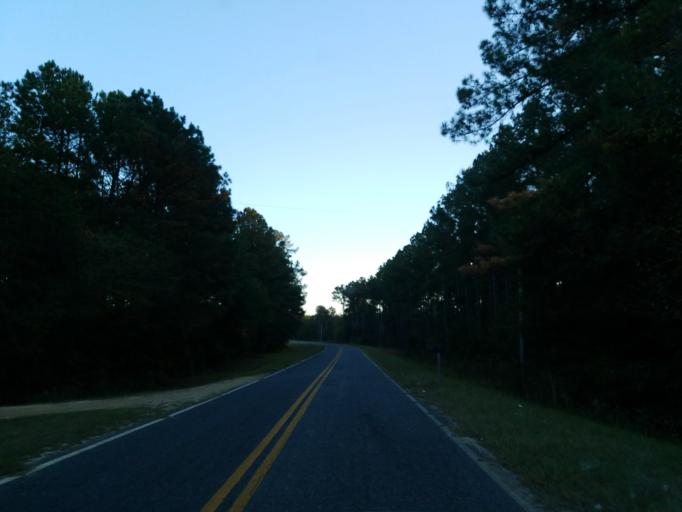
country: US
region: Georgia
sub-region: Ben Hill County
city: Fitzgerald
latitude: 31.6816
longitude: -83.4082
